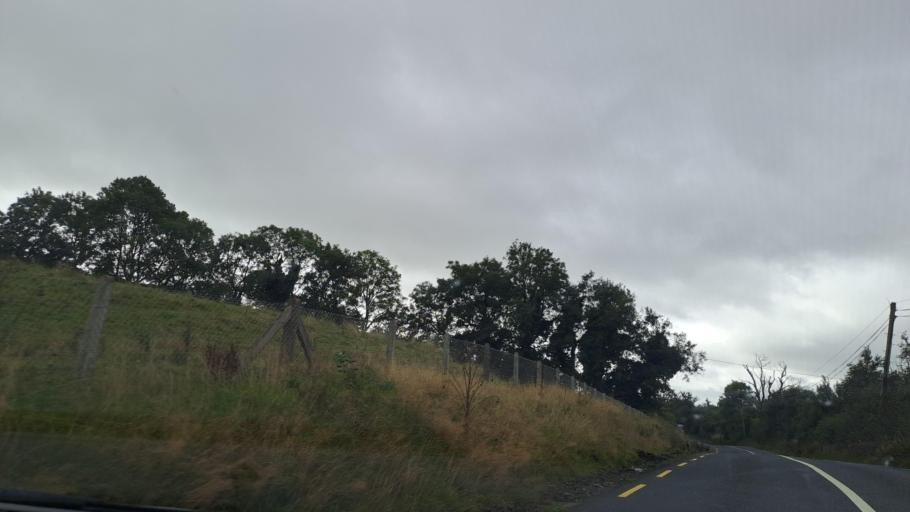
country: IE
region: Ulster
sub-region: An Cabhan
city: Bailieborough
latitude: 53.9419
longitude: -6.9598
